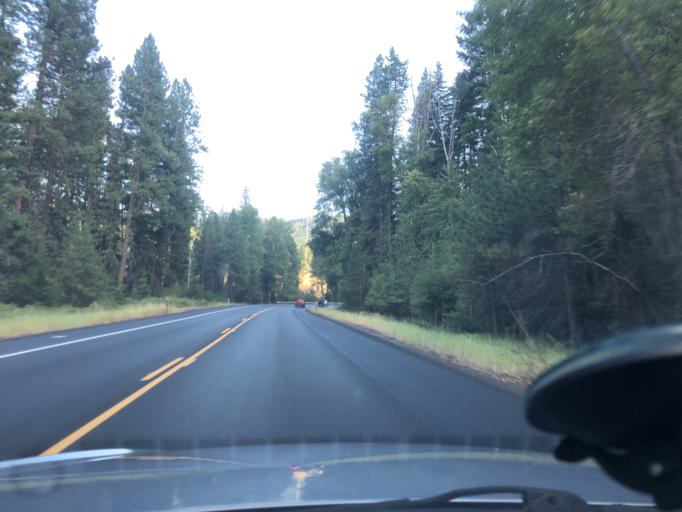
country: US
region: Washington
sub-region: Kittitas County
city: Cle Elum
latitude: 47.2527
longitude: -120.6933
